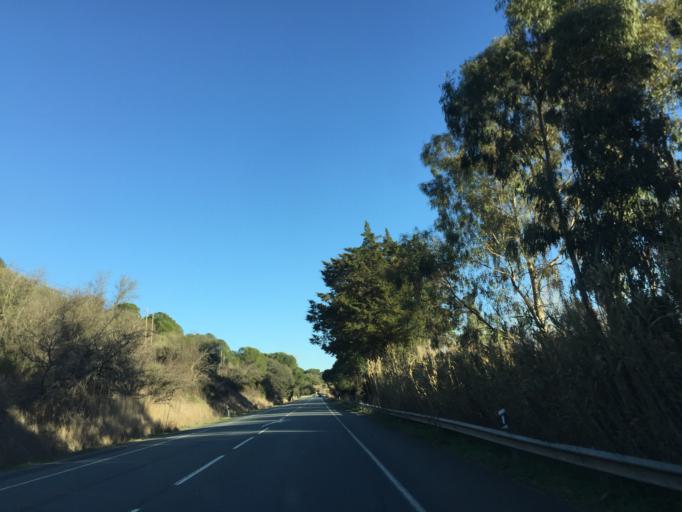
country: PT
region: Setubal
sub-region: Grandola
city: Grandola
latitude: 38.1263
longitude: -8.4615
